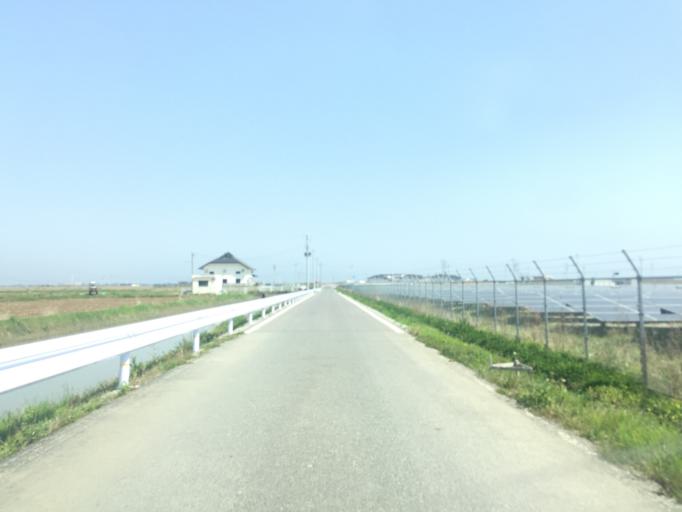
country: JP
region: Miyagi
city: Marumori
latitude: 37.7724
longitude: 140.9775
